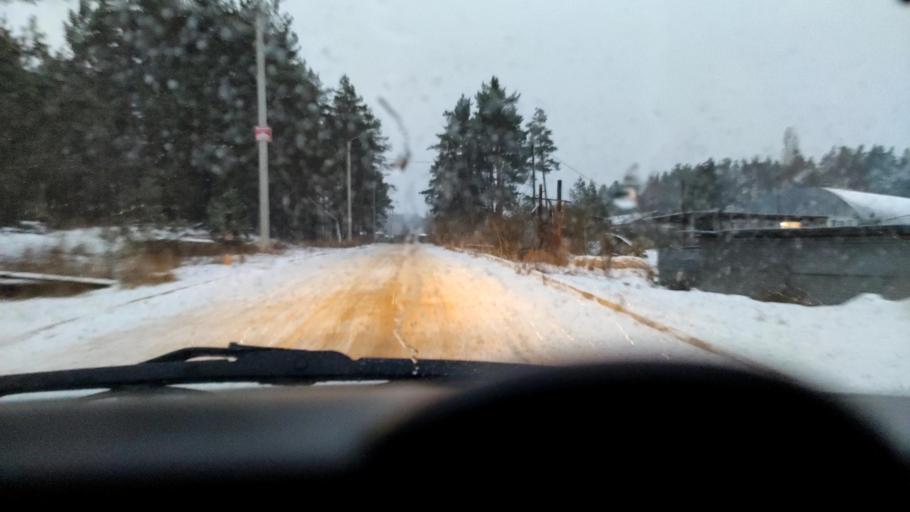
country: RU
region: Voronezj
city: Pridonskoy
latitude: 51.7029
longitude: 39.1057
